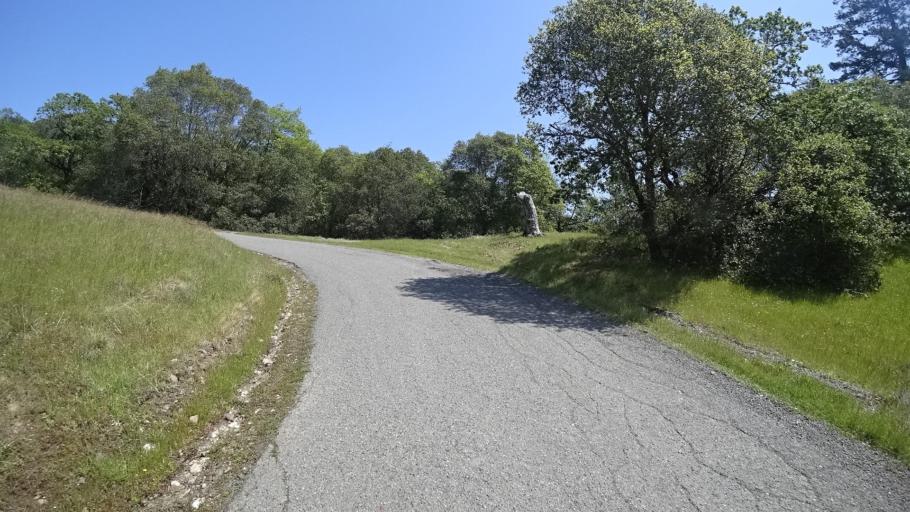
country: US
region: California
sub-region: Humboldt County
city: Redway
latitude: 40.2362
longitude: -123.6326
